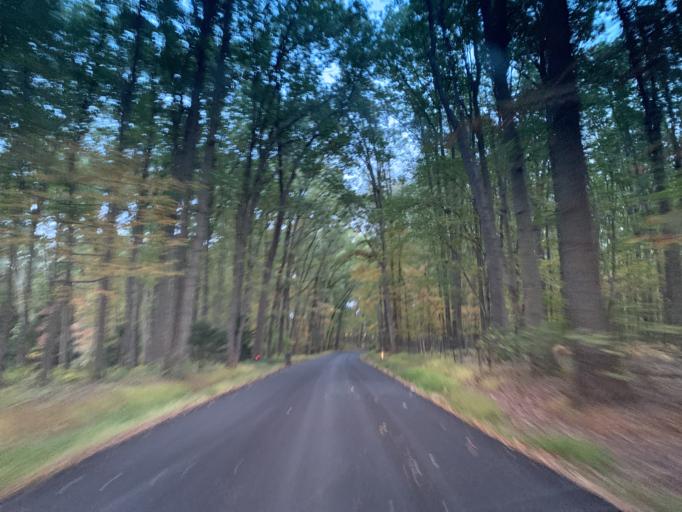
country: US
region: Pennsylvania
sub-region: York County
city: Stewartstown
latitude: 39.6725
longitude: -76.6299
